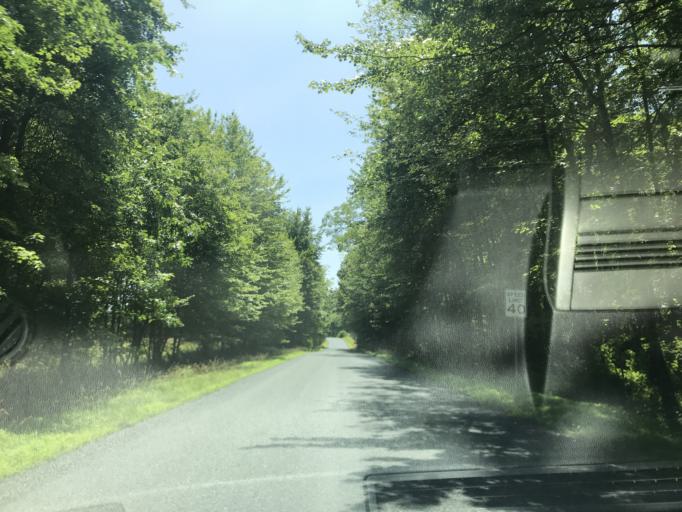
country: US
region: Maryland
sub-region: Harford County
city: Bel Air South
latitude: 39.5462
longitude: -76.2664
